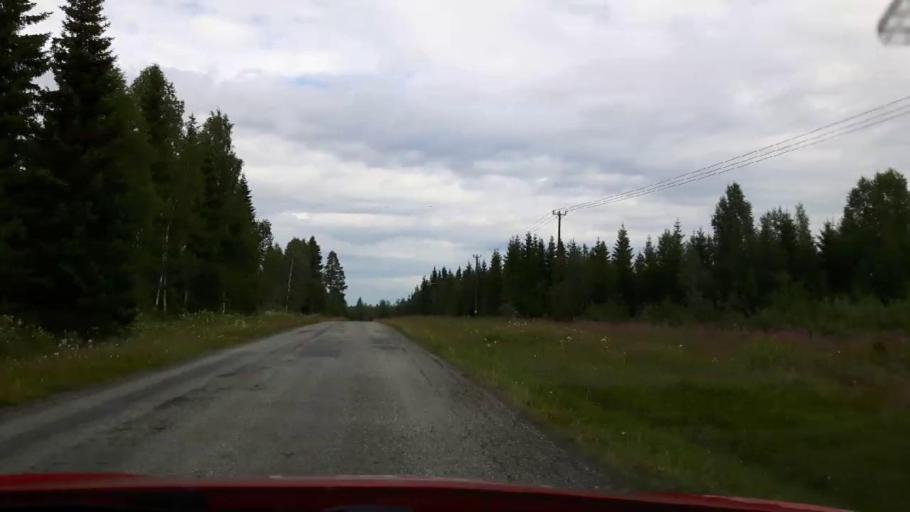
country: SE
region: Jaemtland
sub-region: Stroemsunds Kommun
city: Stroemsund
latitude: 63.5333
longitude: 15.3542
